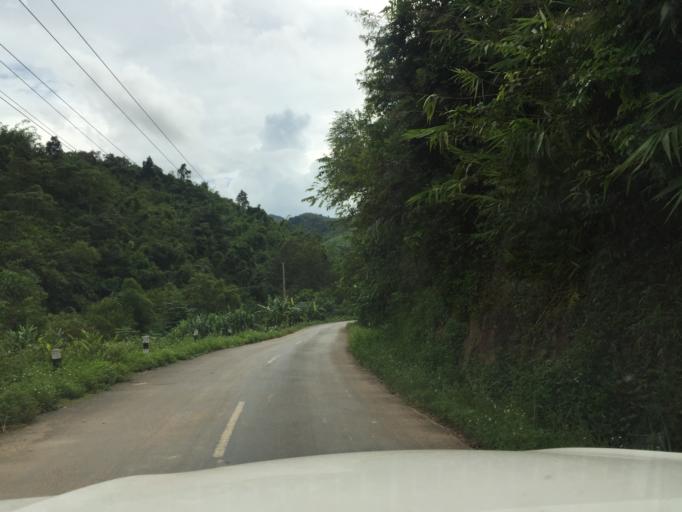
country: LA
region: Phongsali
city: Khoa
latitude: 21.1054
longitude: 102.2408
